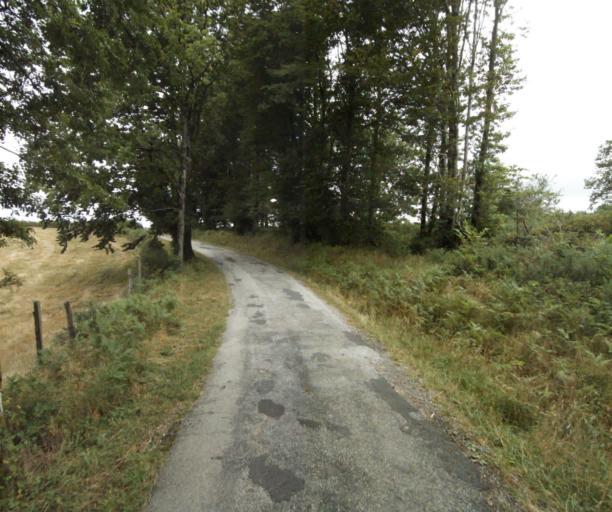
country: FR
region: Midi-Pyrenees
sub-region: Departement du Tarn
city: Soreze
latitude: 43.4234
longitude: 2.0989
